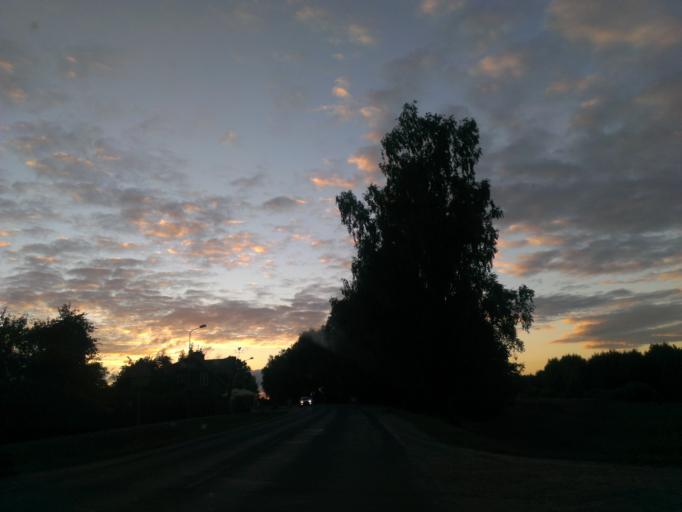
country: LV
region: Vecumnieki
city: Vecumnieki
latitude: 56.6084
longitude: 24.5189
